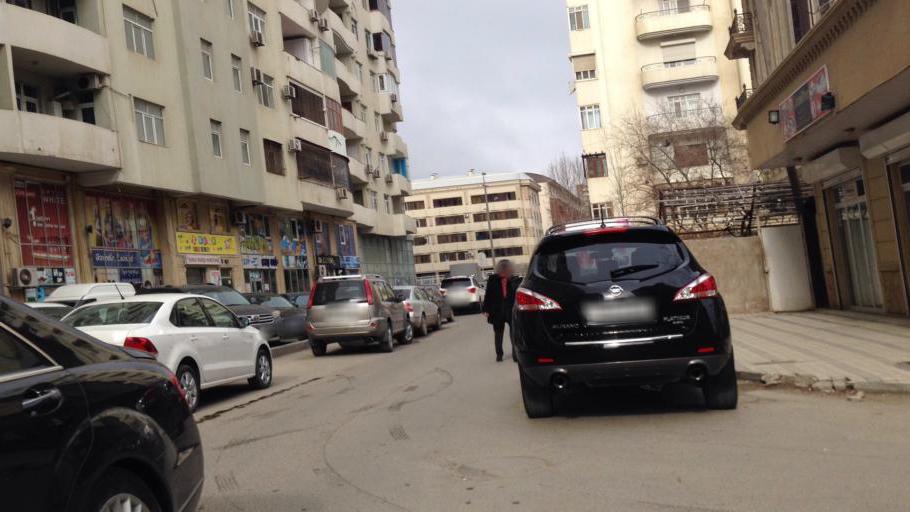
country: AZ
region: Baki
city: Bilajari
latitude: 40.4114
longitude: 49.8437
